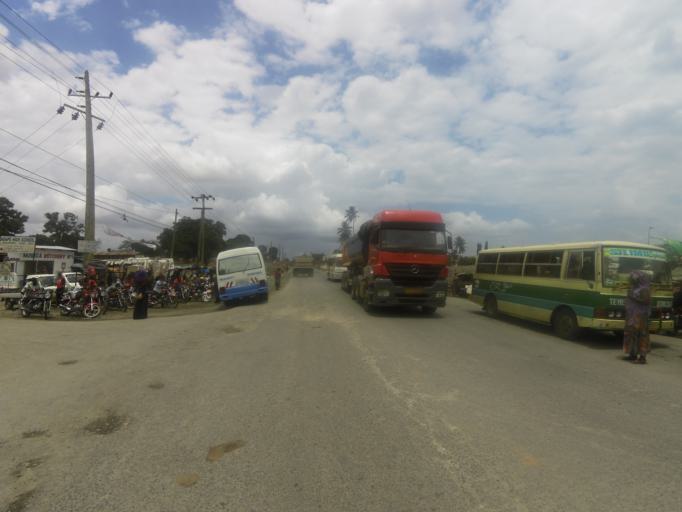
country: TZ
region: Pwani
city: Vikindu
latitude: -6.9422
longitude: 39.2787
